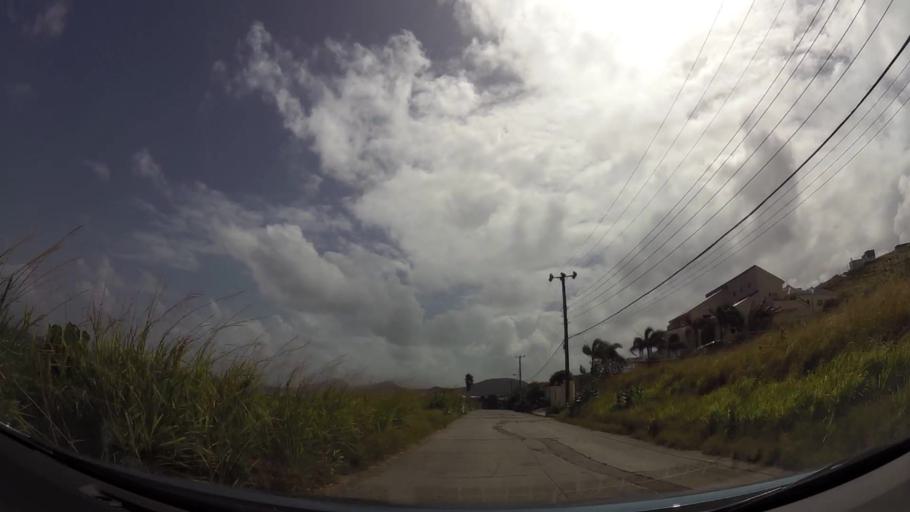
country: KN
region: Saint Peter Basseterre
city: Monkey Hill
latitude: 17.3060
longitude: -62.6940
